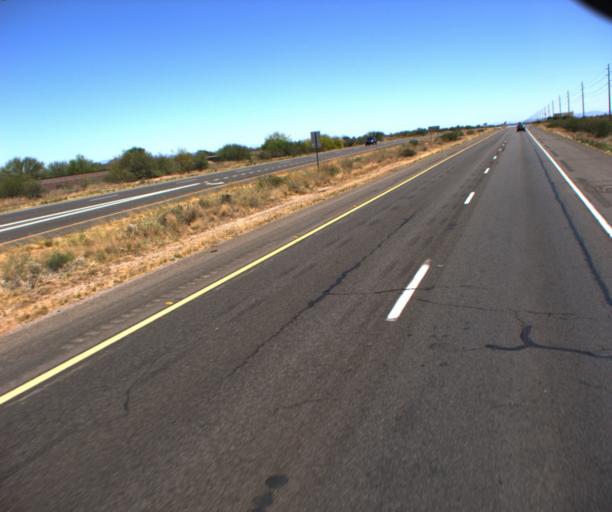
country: US
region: Arizona
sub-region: Maricopa County
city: Sun City West
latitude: 33.7399
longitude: -112.4802
